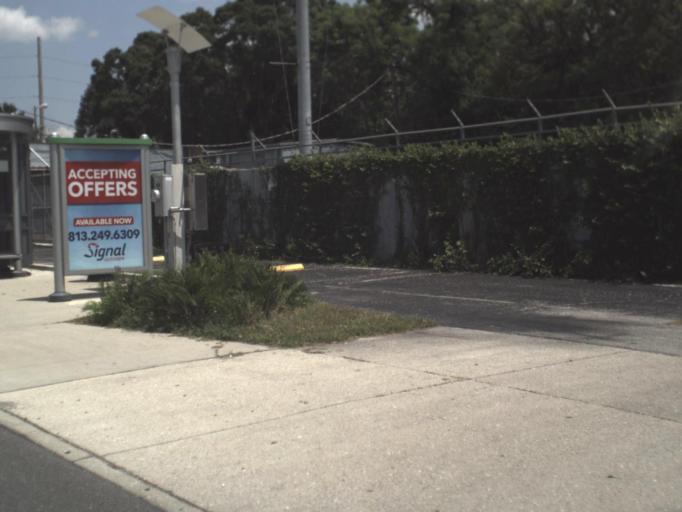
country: US
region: Florida
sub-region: Hillsborough County
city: Tampa
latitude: 27.9769
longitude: -82.4511
